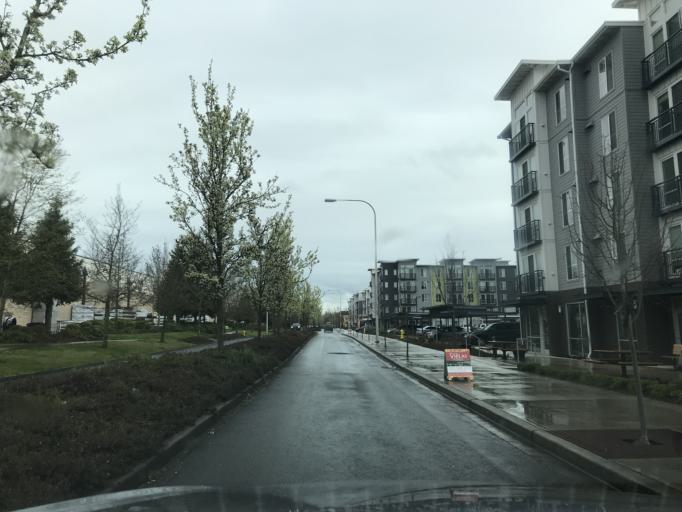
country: US
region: Washington
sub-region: King County
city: Auburn
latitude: 47.3194
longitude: -122.2288
